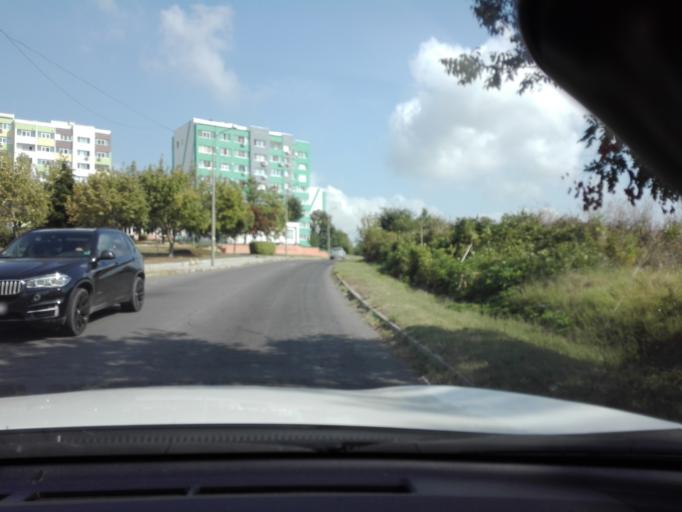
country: BG
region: Burgas
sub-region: Obshtina Burgas
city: Burgas
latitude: 42.4549
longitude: 27.4236
